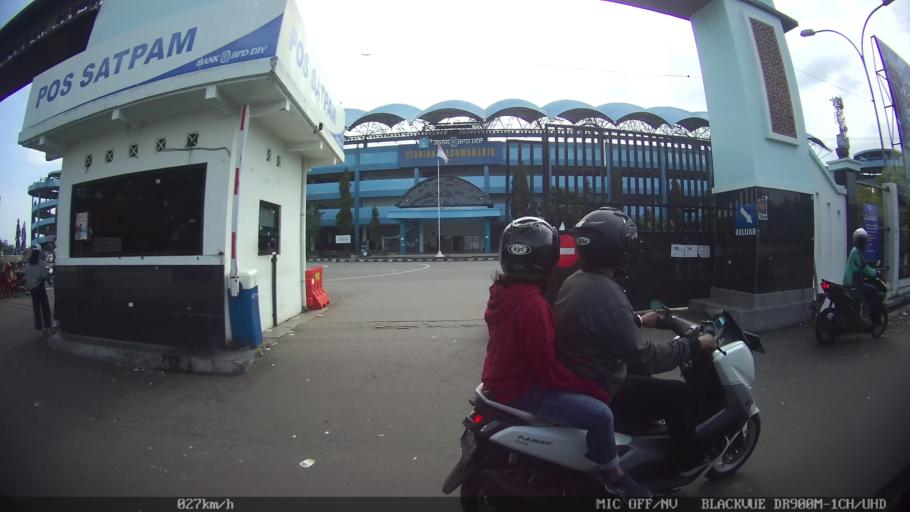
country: ID
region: Daerah Istimewa Yogyakarta
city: Depok
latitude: -7.7509
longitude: 110.4195
